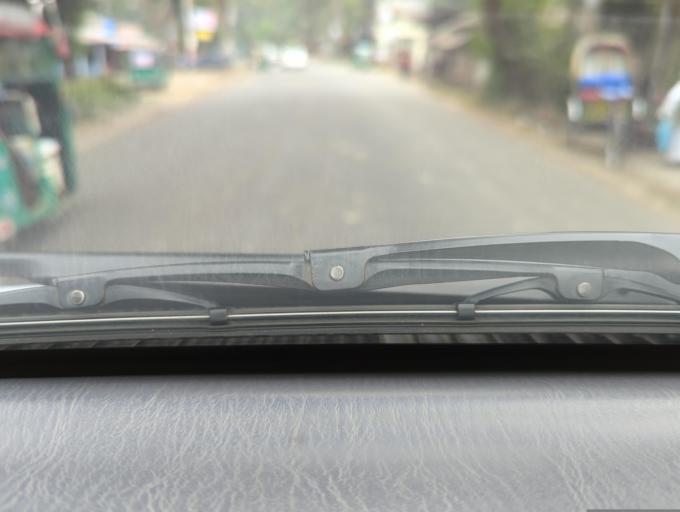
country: BD
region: Sylhet
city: Maulavi Bazar
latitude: 24.5112
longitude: 91.7258
